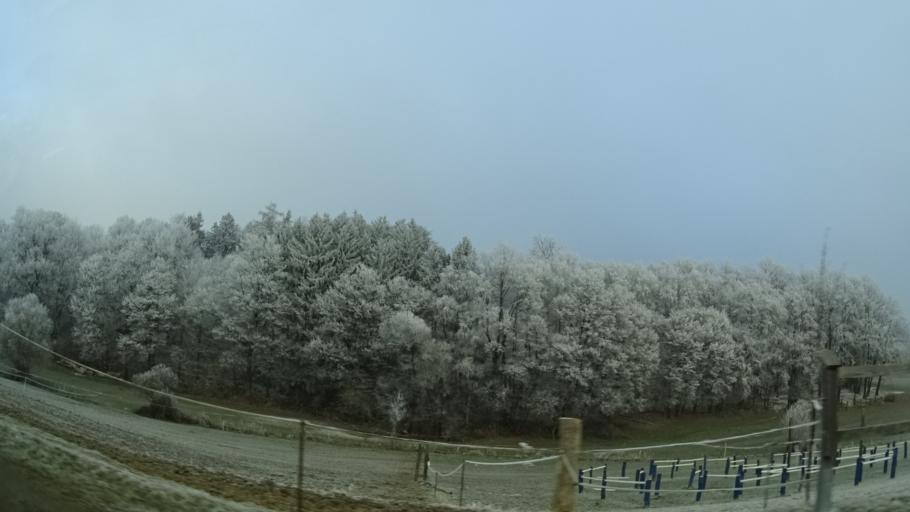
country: DE
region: Hesse
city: Lutzelbach
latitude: 49.7638
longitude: 8.7366
